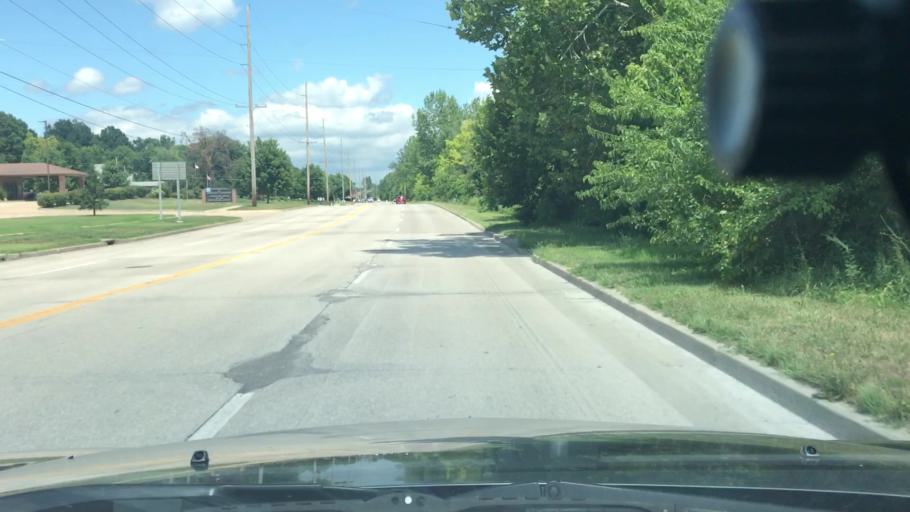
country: US
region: Missouri
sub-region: Saint Charles County
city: Saint Charles
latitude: 38.7562
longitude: -90.4998
